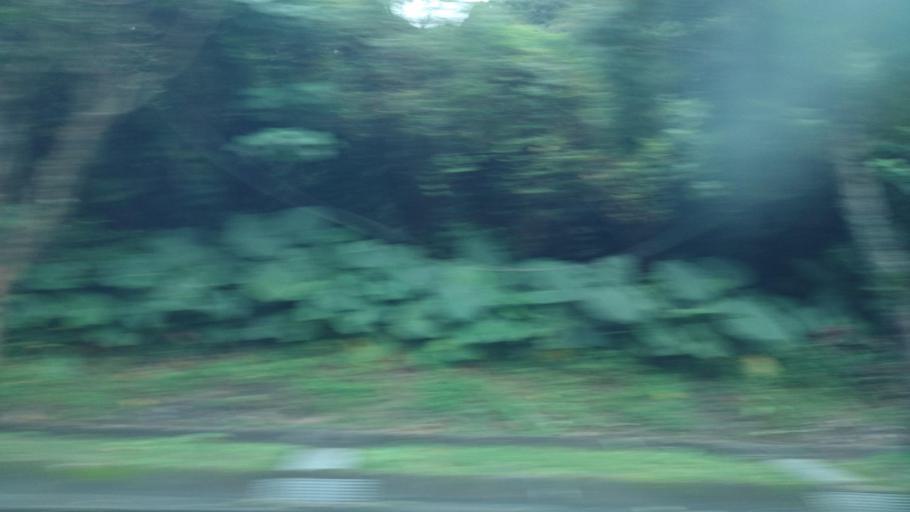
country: TW
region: Taiwan
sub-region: Yilan
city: Yilan
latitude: 24.6062
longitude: 121.8371
